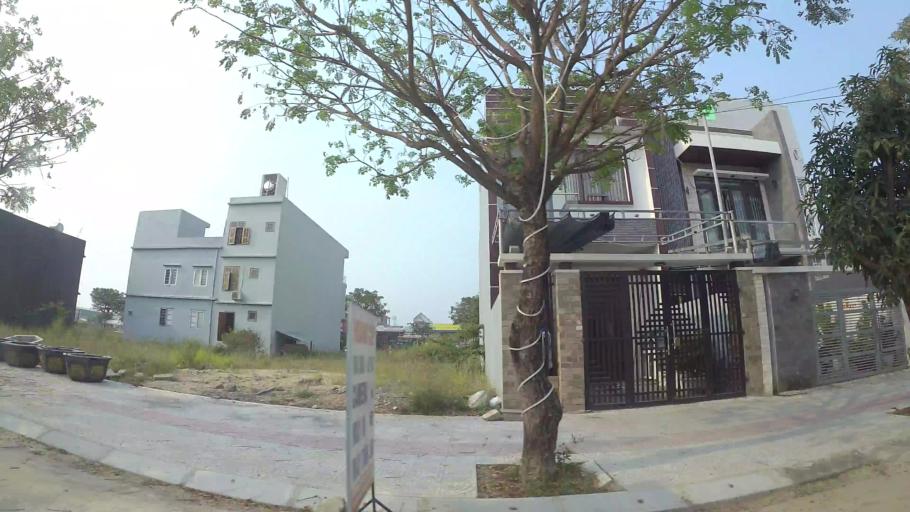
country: VN
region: Da Nang
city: Cam Le
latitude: 16.0042
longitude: 108.2250
